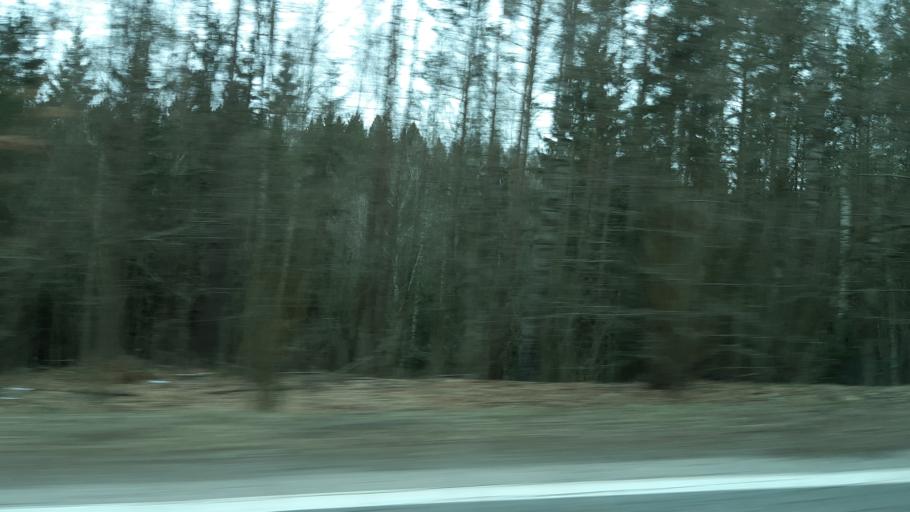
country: PL
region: Podlasie
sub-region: Suwalki
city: Suwalki
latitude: 54.2854
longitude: 22.9511
